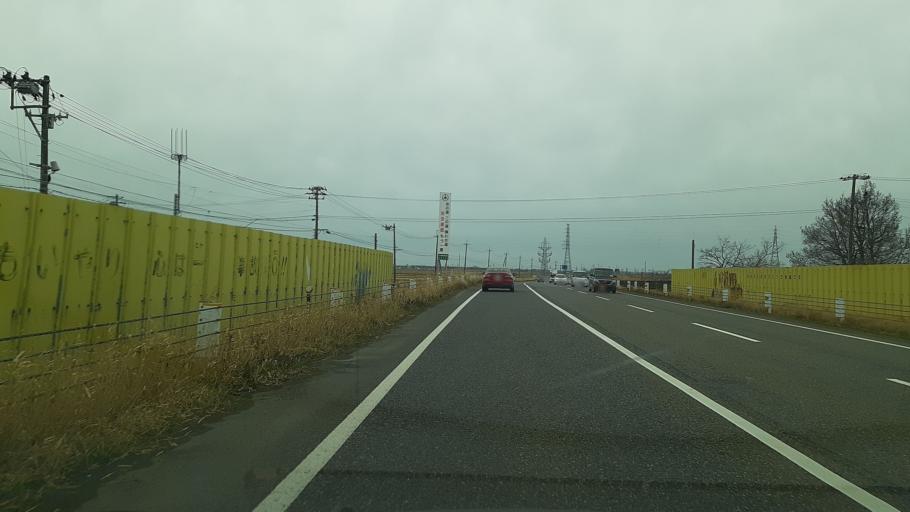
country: JP
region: Niigata
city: Niitsu-honcho
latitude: 37.7988
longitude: 139.1051
